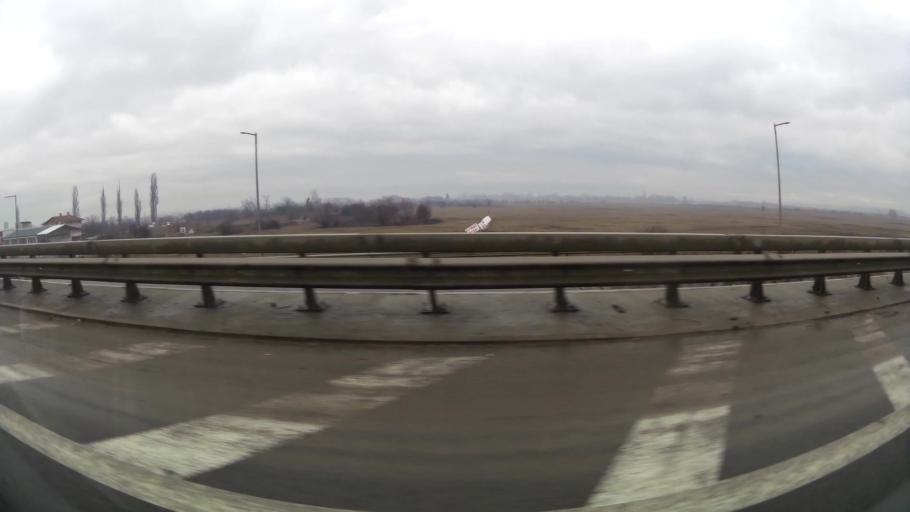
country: BG
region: Sofia-Capital
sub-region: Stolichna Obshtina
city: Sofia
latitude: 42.7275
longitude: 23.3809
